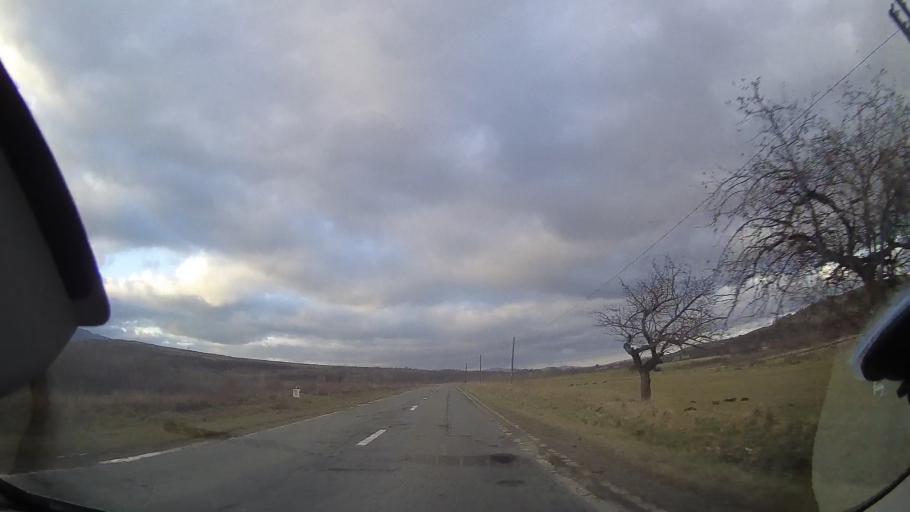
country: RO
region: Cluj
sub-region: Comuna Calatele
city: Calatele
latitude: 46.7908
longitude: 22.9979
